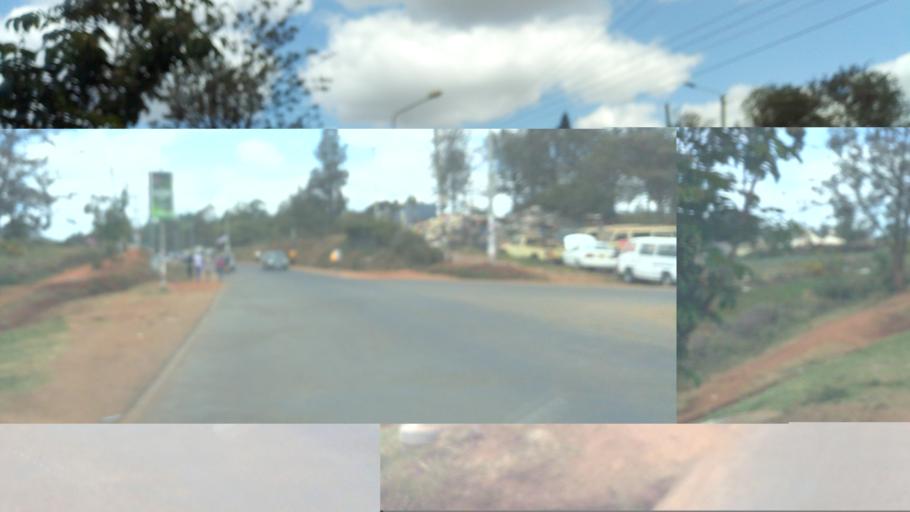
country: KE
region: Nairobi Area
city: Nairobi
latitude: -1.3295
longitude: 36.7801
